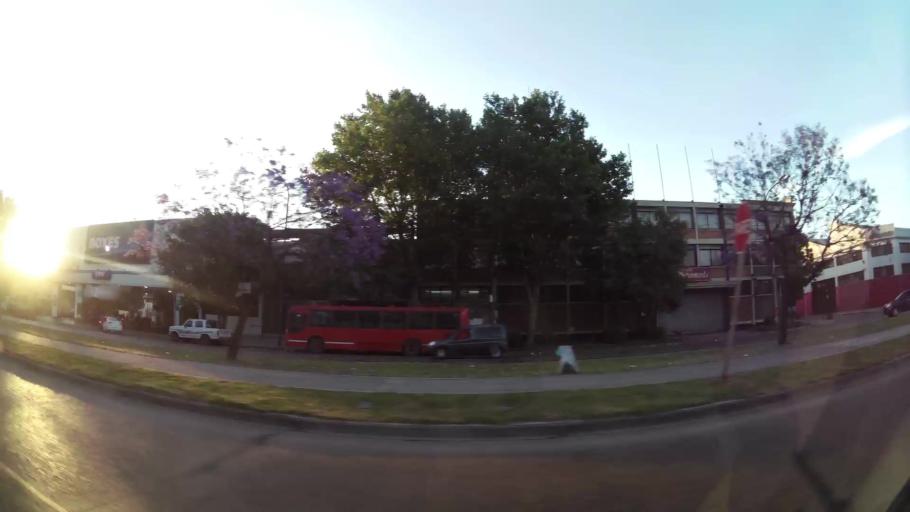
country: AR
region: Buenos Aires F.D.
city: Villa Lugano
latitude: -34.6961
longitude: -58.4678
